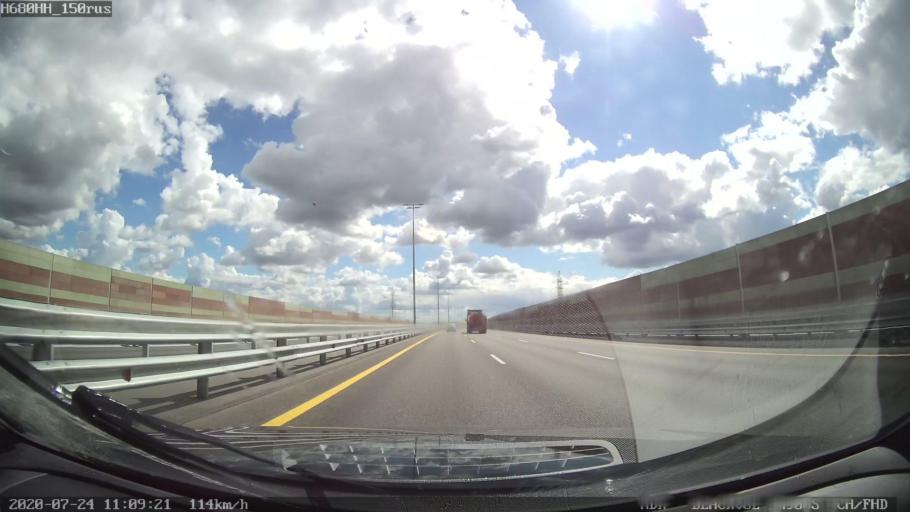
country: RU
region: St.-Petersburg
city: Tyarlevo
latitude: 59.7498
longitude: 30.4718
